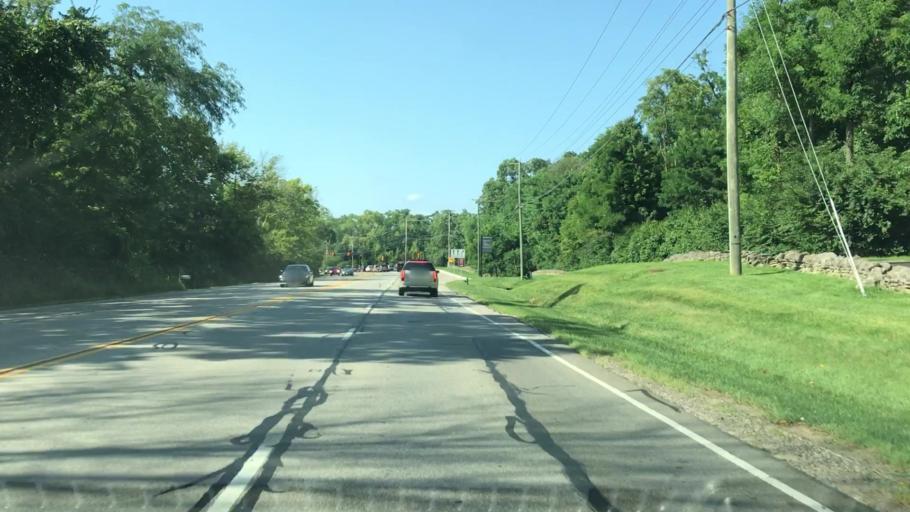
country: US
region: Ohio
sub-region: Franklin County
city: Dublin
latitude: 40.1186
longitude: -83.1095
